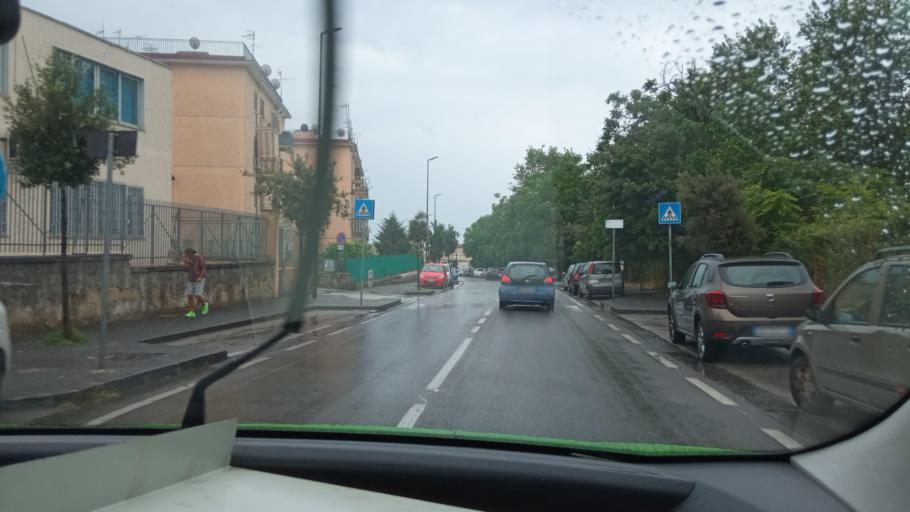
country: IT
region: Campania
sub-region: Provincia di Napoli
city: Pozzuoli
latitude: 40.8354
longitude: 14.1158
